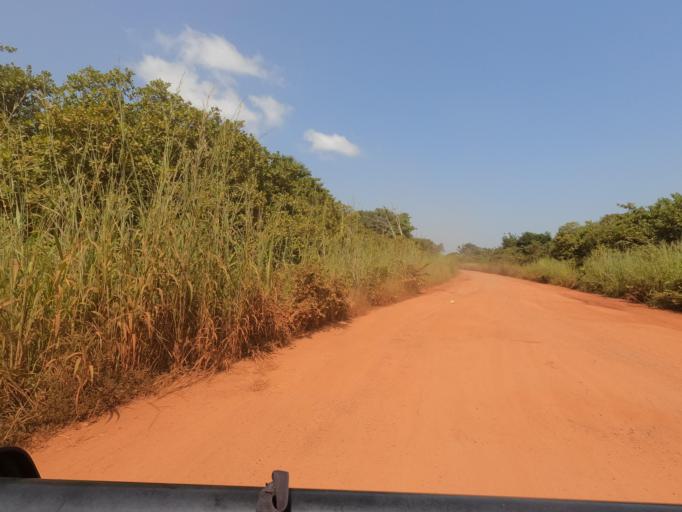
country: GW
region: Oio
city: Bissora
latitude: 12.3493
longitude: -15.7641
